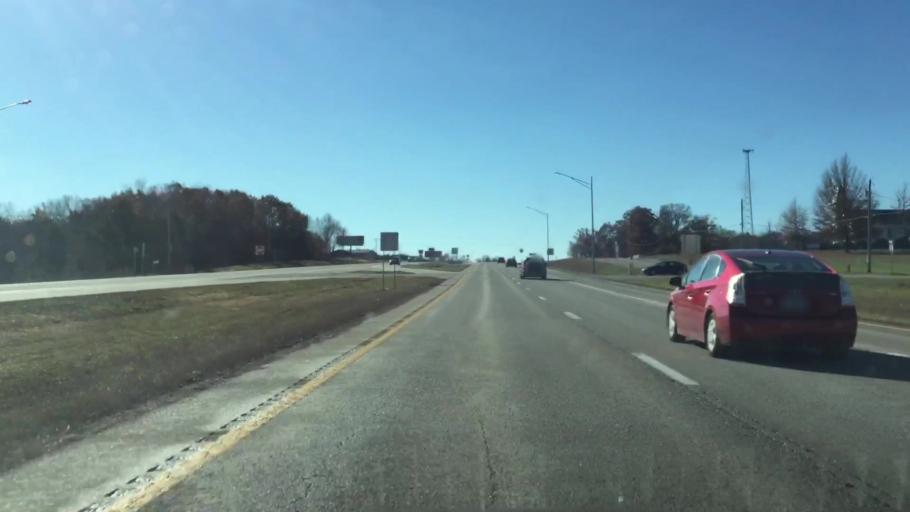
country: US
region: Missouri
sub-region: Cole County
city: Wardsville
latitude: 38.4464
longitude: -92.3028
